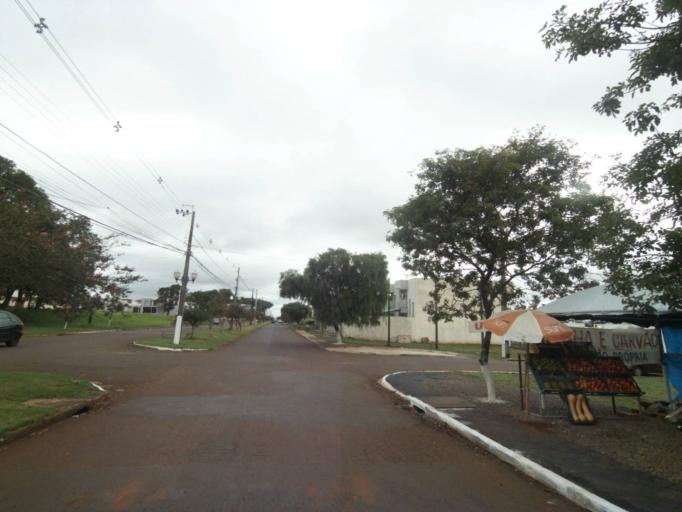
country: BR
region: Parana
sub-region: Campo Mourao
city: Campo Mourao
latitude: -24.0393
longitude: -52.3643
